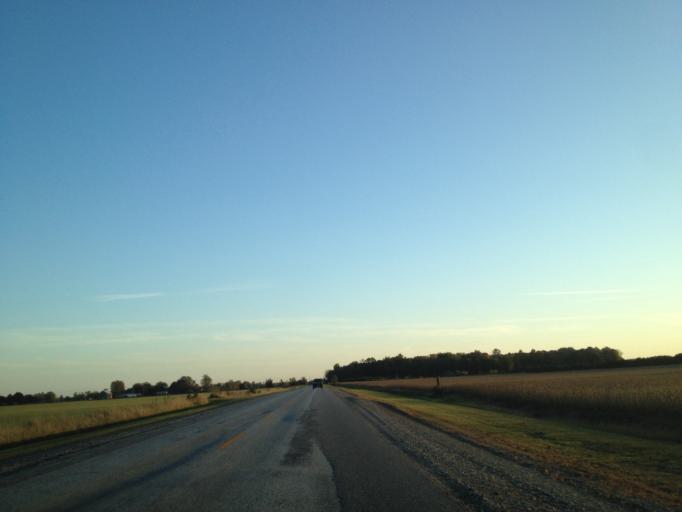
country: US
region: Michigan
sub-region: Wayne County
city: Grosse Pointe Farms
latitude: 42.0637
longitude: -82.5156
